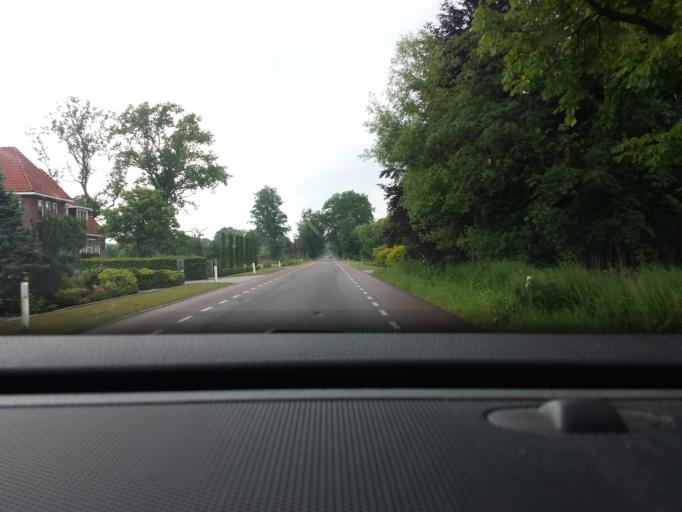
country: NL
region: Gelderland
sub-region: Berkelland
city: Eibergen
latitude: 52.0536
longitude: 6.6830
